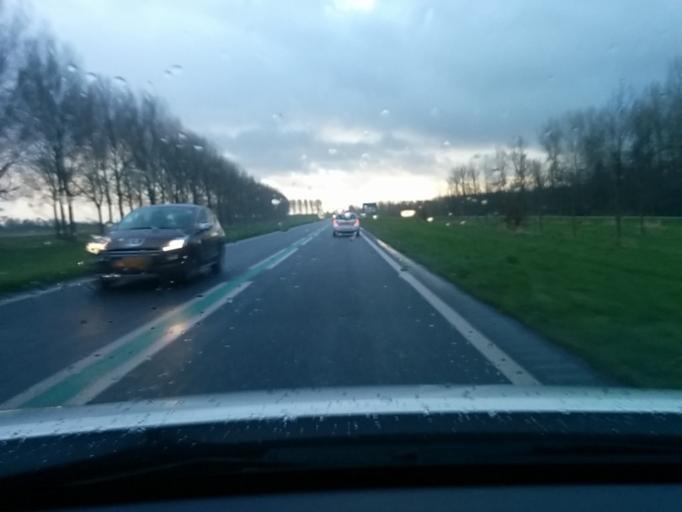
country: NL
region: Gelderland
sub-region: Gemeente Nijkerk
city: Nijkerk
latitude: 52.2730
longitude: 5.4660
